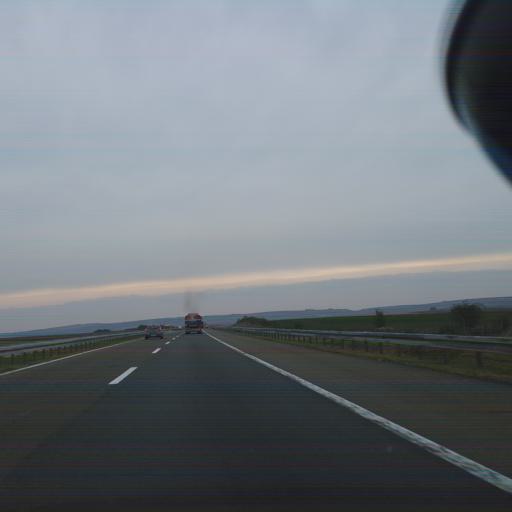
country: RS
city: Krcedin
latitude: 45.1100
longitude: 20.1041
